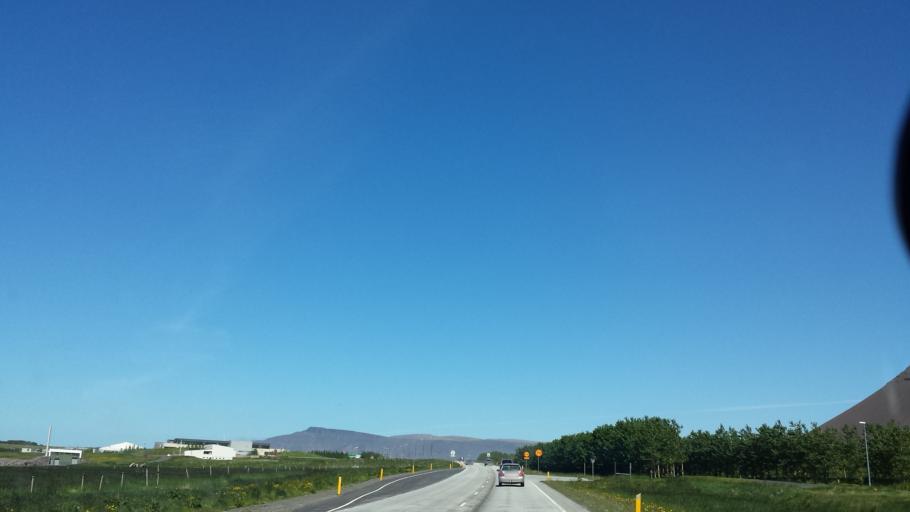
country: IS
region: Capital Region
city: Reykjavik
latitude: 64.2337
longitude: -21.8187
